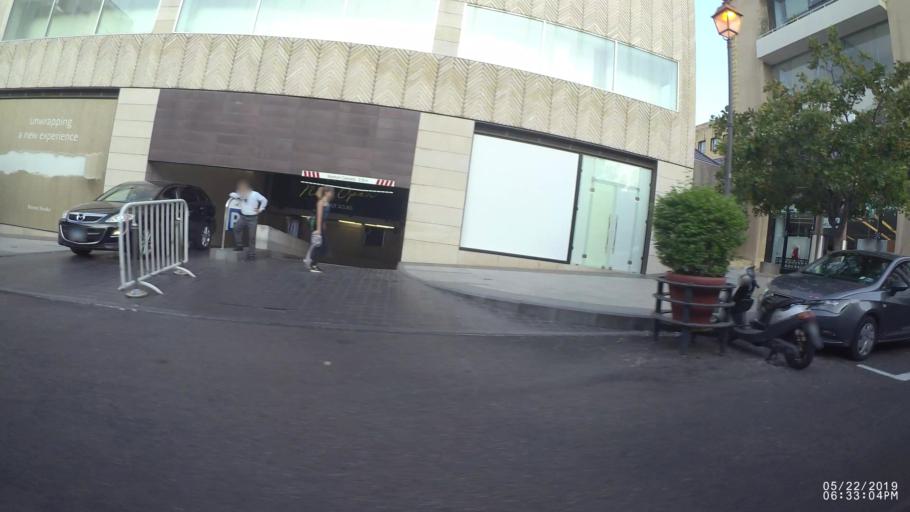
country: LB
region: Beyrouth
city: Beirut
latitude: 33.8996
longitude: 35.5028
